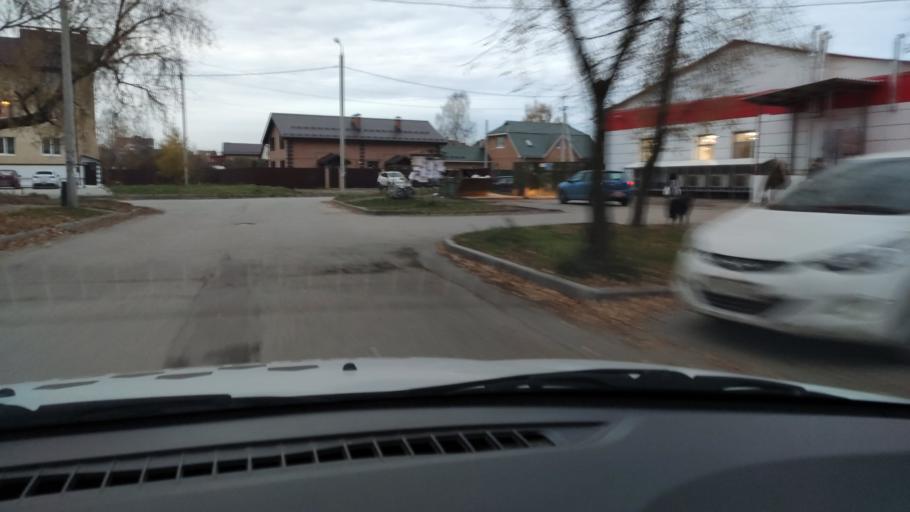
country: RU
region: Perm
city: Kondratovo
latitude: 58.0396
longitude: 56.1116
